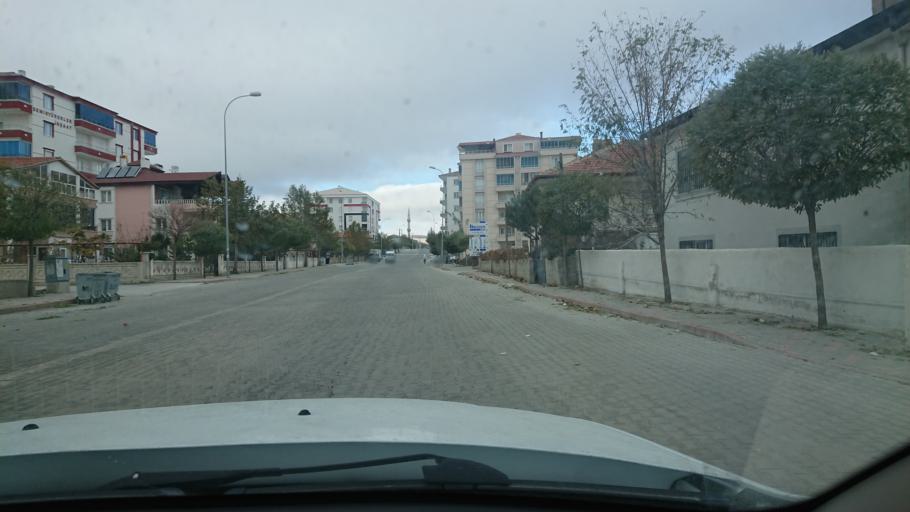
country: TR
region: Aksaray
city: Ortakoy
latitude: 38.7408
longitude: 34.0353
